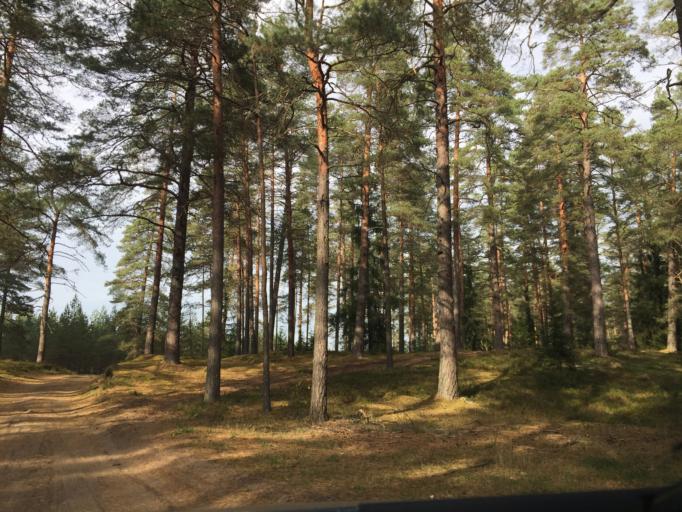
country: LV
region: Garkalne
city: Garkalne
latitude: 56.9502
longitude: 24.4289
